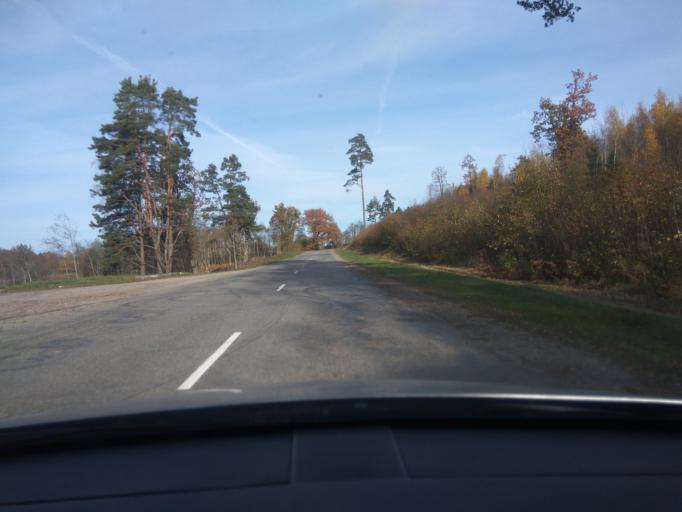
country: LV
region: Alsunga
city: Alsunga
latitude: 57.0082
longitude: 21.6801
